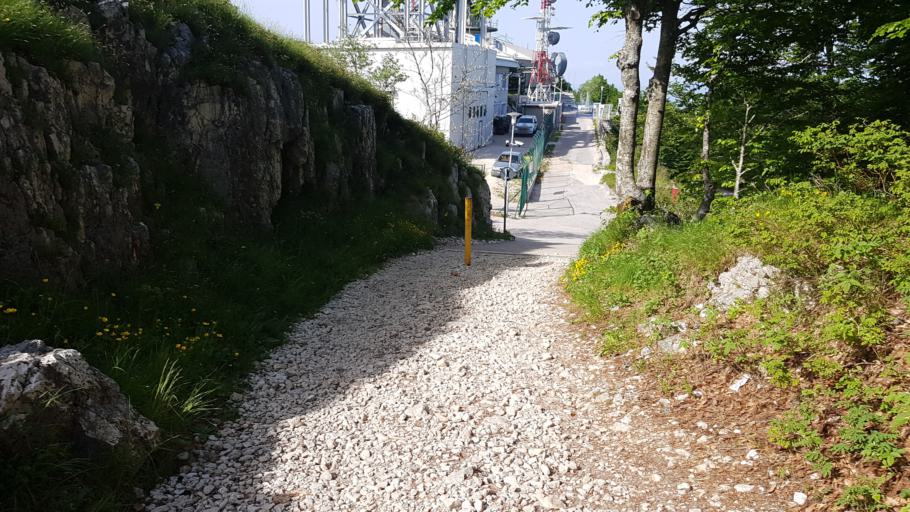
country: HR
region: Istarska
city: Lovran
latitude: 45.2861
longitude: 14.2022
